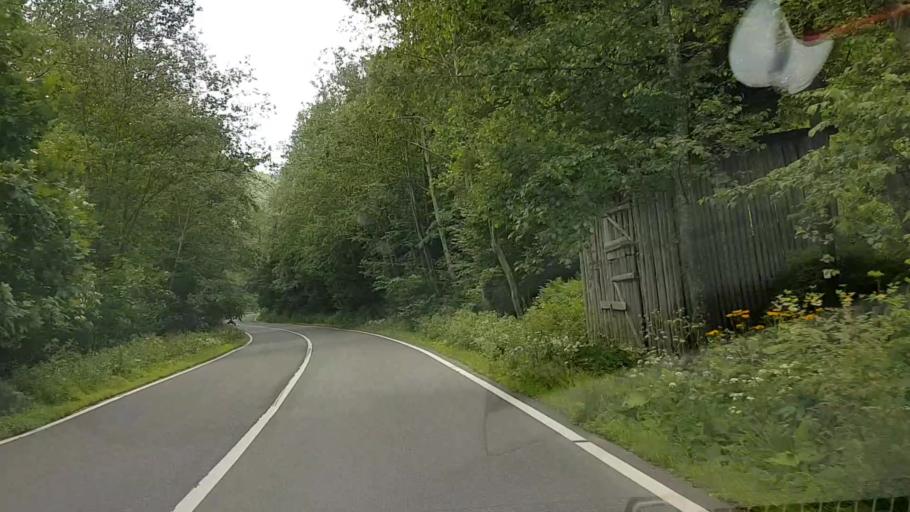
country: RO
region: Suceava
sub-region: Comuna Crucea
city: Crucea
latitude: 47.3258
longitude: 25.6220
